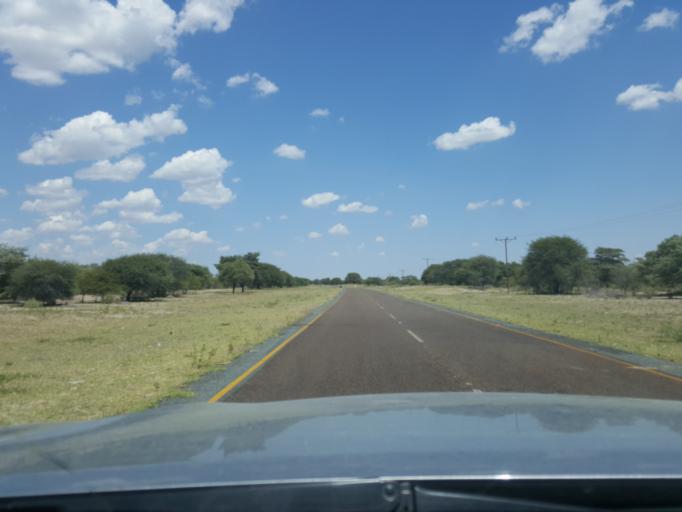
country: BW
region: North West
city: Maun
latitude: -20.1603
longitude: 23.2653
